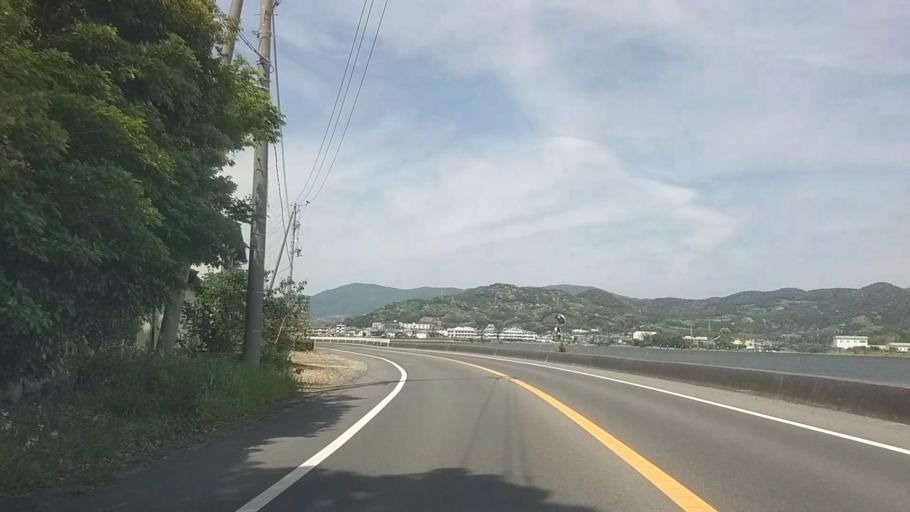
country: JP
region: Shizuoka
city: Kosai-shi
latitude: 34.7955
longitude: 137.5486
